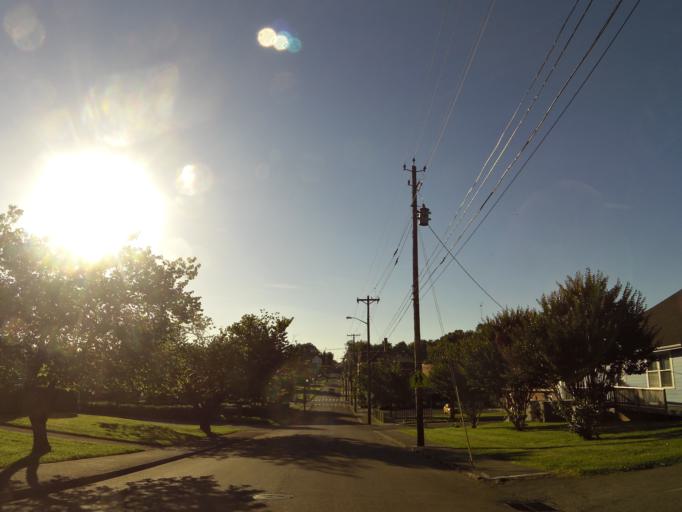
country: US
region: Tennessee
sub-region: Knox County
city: Knoxville
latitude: 35.9673
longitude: -83.9369
